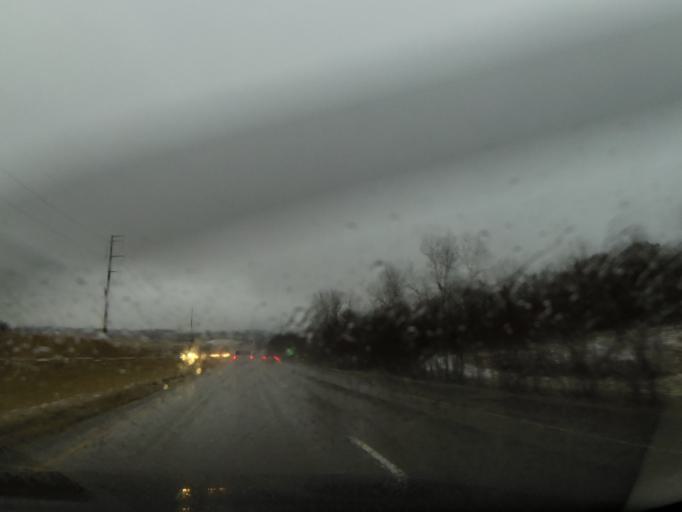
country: US
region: Minnesota
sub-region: Goodhue County
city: Zumbrota
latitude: 44.3268
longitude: -92.7195
